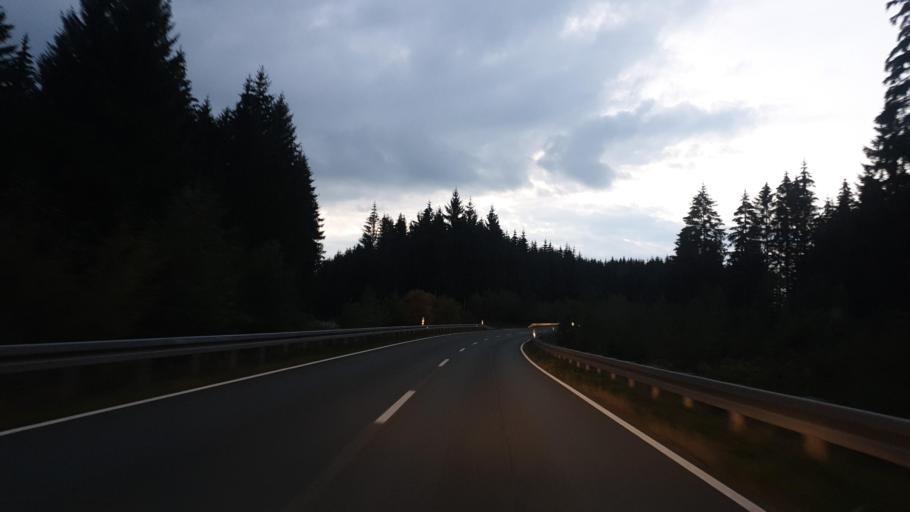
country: DE
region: Saxony
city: Schoenheide
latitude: 50.5057
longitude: 12.4888
